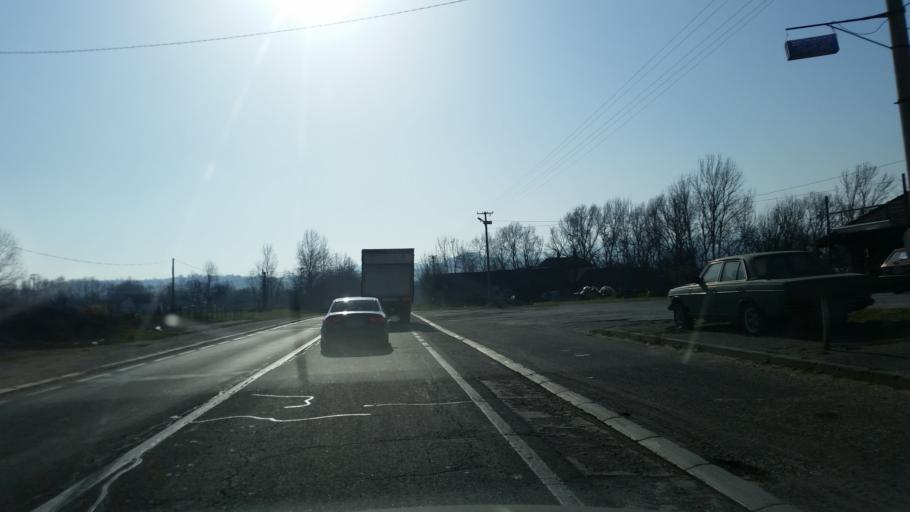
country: RS
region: Central Serbia
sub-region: Kolubarski Okrug
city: Ljig
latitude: 44.2610
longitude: 20.2861
